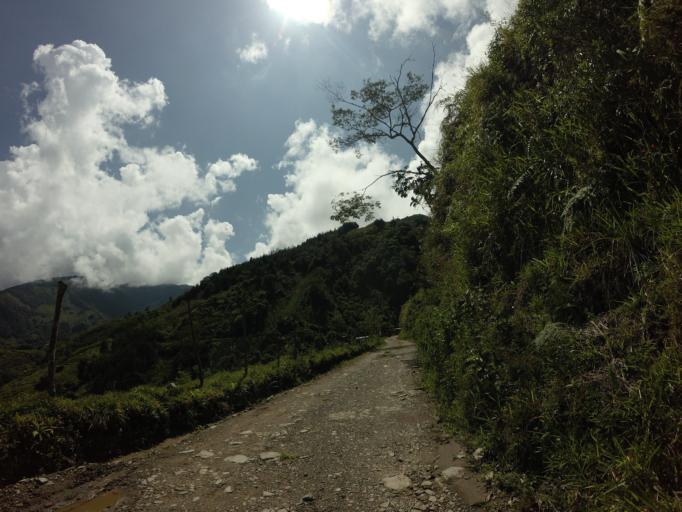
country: CO
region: Caldas
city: Pensilvania
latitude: 5.4700
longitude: -75.1852
